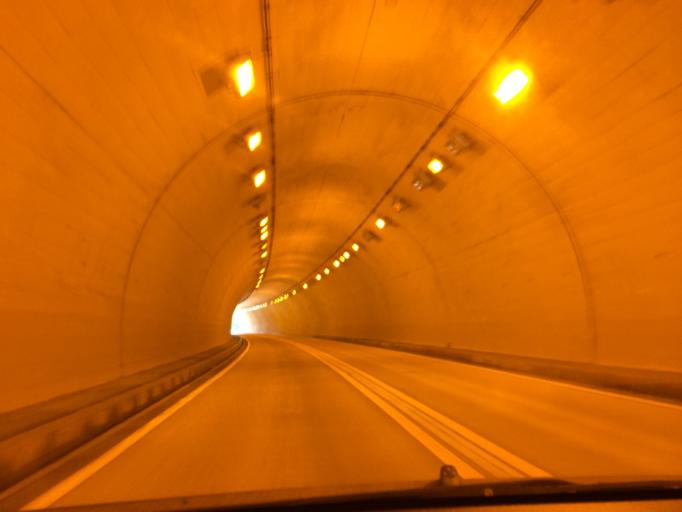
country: JP
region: Tottori
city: Kurayoshi
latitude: 35.3448
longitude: 133.7485
